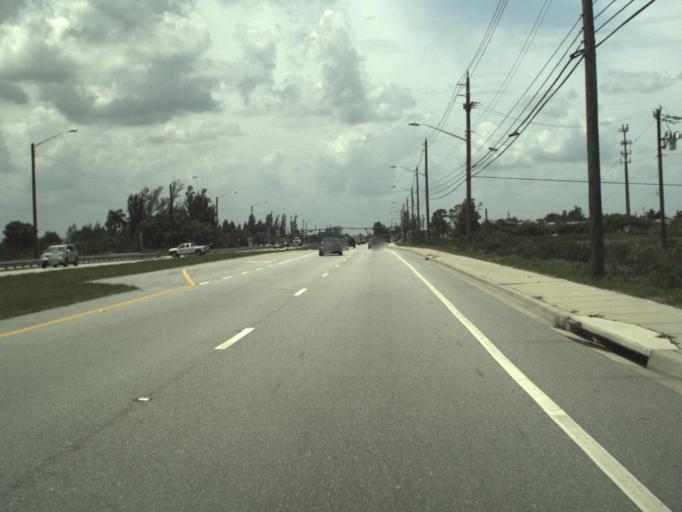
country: US
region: Florida
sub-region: Palm Beach County
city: Villages of Oriole
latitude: 26.4539
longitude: -80.1827
